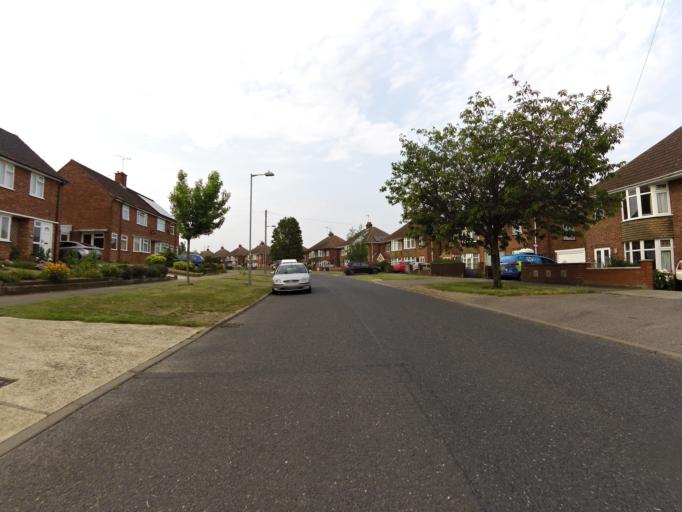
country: GB
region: England
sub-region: Suffolk
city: Ipswich
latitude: 52.0767
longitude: 1.1388
